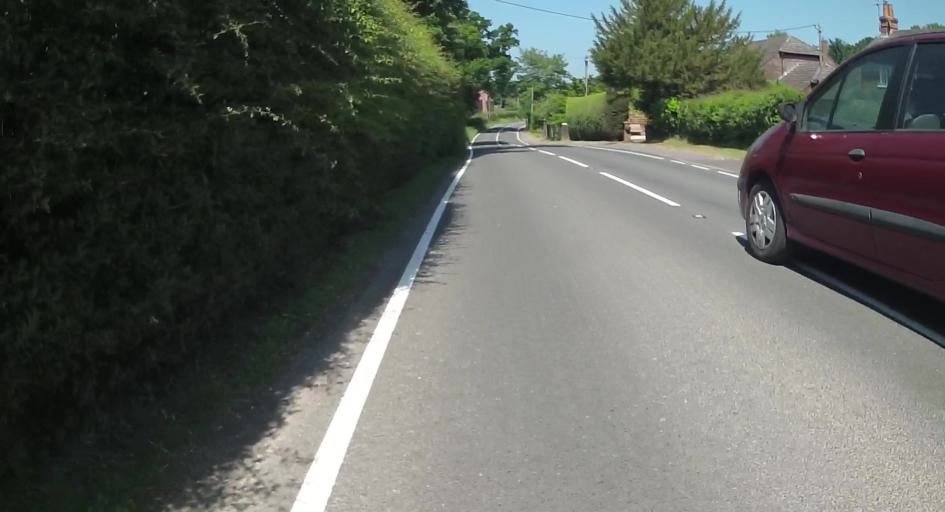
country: GB
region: England
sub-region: Hampshire
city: Kingsclere
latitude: 51.3510
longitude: -1.2048
